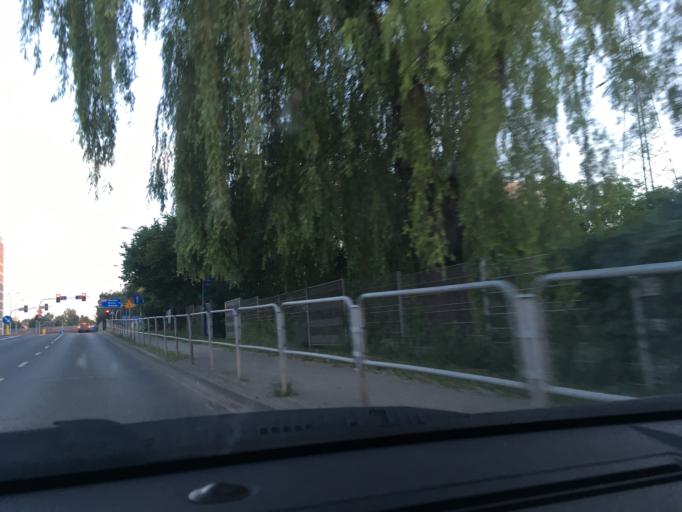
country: PL
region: Silesian Voivodeship
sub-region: Katowice
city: Katowice
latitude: 50.2492
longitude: 19.0261
